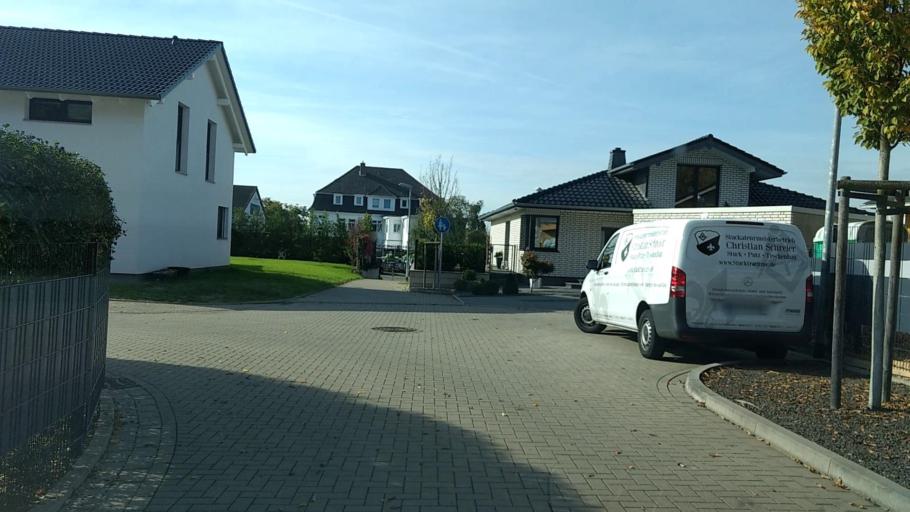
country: DE
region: North Rhine-Westphalia
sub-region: Regierungsbezirk Koln
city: Kerpen
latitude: 50.9337
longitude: 6.7020
